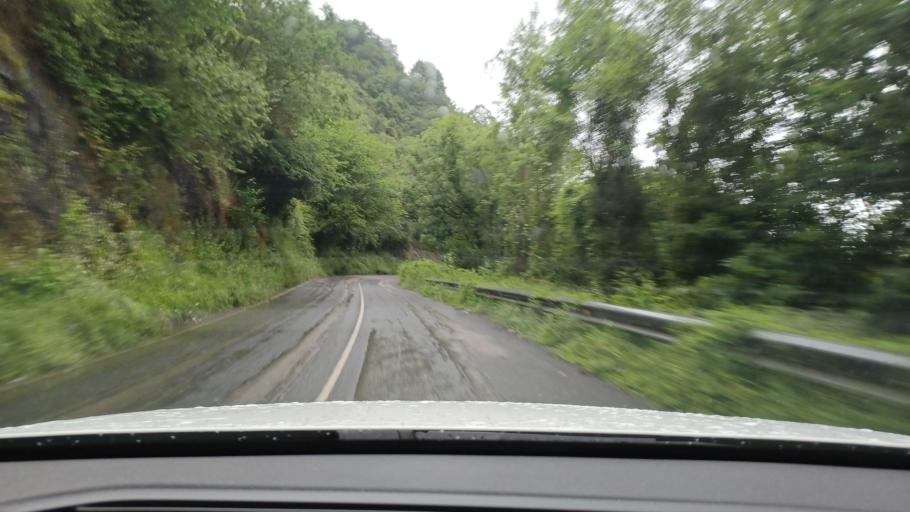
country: ES
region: Asturias
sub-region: Province of Asturias
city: Castandiello
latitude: 43.3104
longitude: -5.9184
